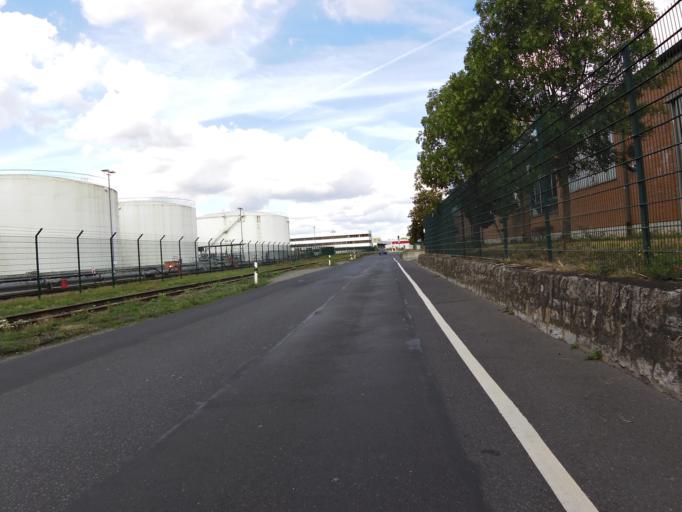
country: DE
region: Bavaria
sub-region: Regierungsbezirk Unterfranken
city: Zell am Main
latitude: 49.8096
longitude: 9.8778
